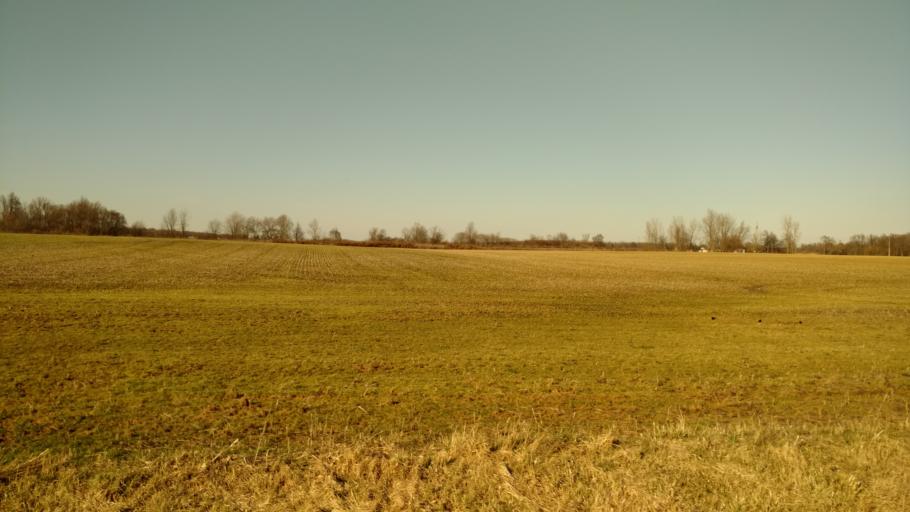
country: US
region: Ohio
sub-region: Crawford County
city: Galion
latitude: 40.6983
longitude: -82.8524
